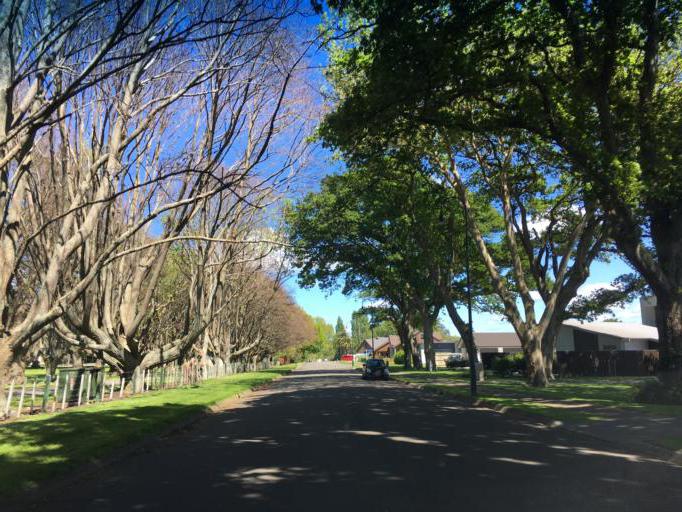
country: NZ
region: Manawatu-Wanganui
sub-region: Palmerston North City
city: Palmerston North
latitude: -40.3795
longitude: 175.5769
